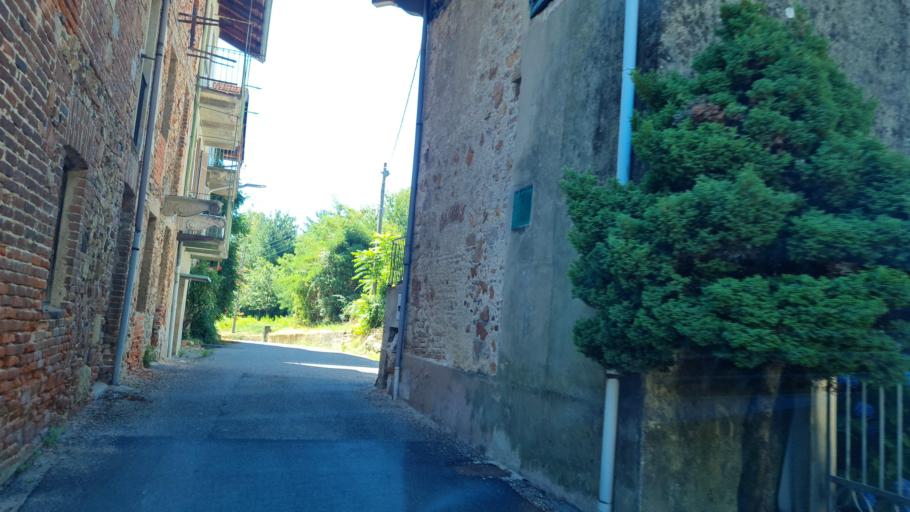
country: IT
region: Piedmont
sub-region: Provincia di Biella
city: Masserano
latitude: 45.5942
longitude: 8.2164
